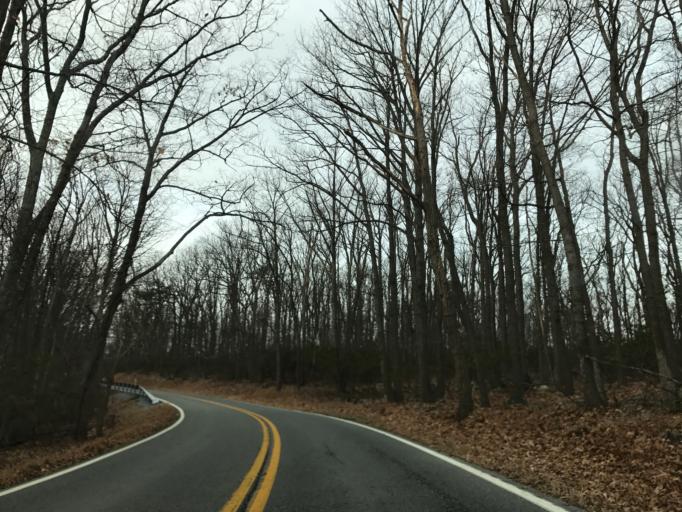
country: US
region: Maryland
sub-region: Frederick County
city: Braddock Heights
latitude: 39.4605
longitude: -77.4894
